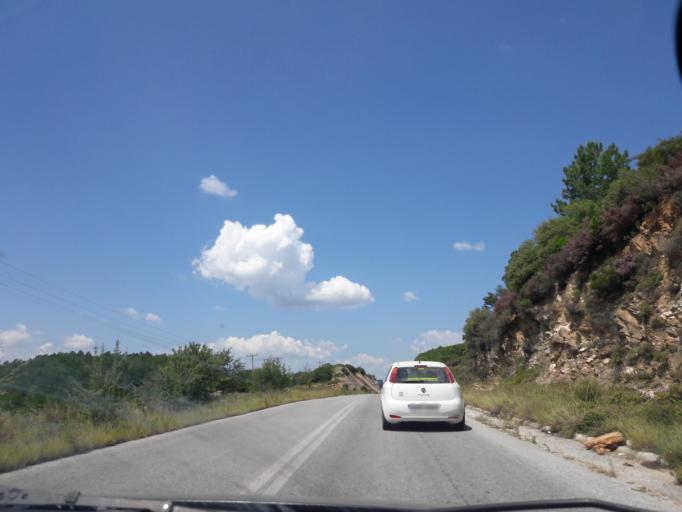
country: GR
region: Central Macedonia
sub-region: Nomos Chalkidikis
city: Polygyros
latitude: 40.3674
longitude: 23.4616
